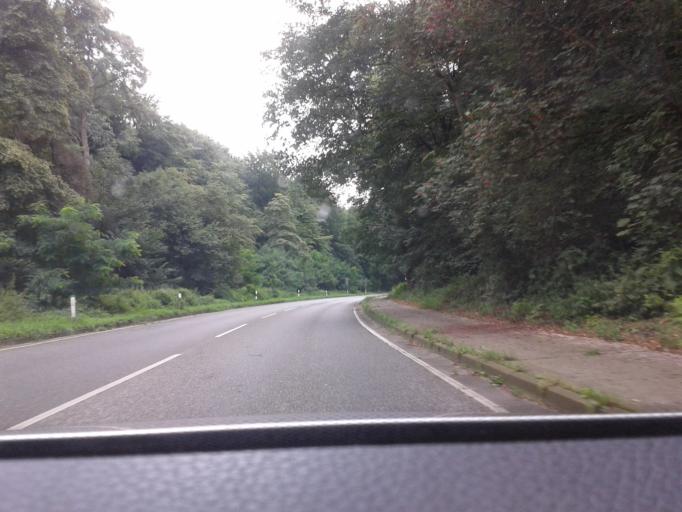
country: DE
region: North Rhine-Westphalia
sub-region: Regierungsbezirk Dusseldorf
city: Duisburg
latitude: 51.4369
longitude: 6.8103
